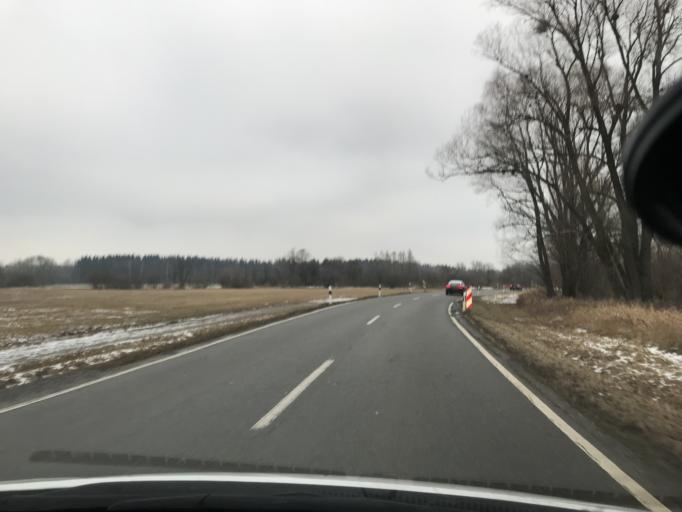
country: DE
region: Bavaria
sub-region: Upper Bavaria
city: Bad Feilnbach
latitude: 47.7978
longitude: 12.0155
